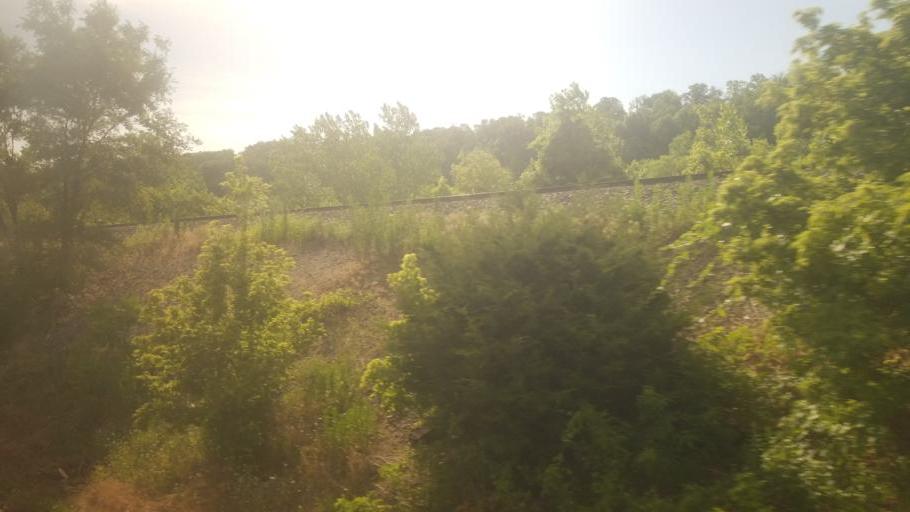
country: US
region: Kansas
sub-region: Johnson County
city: Shawnee
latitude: 39.0715
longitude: -94.7356
